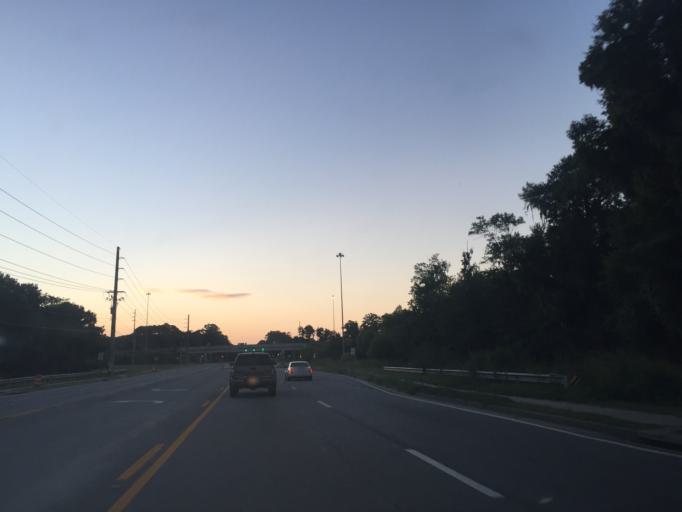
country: US
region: Georgia
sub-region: Chatham County
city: Isle of Hope
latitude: 31.9903
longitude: -81.0872
